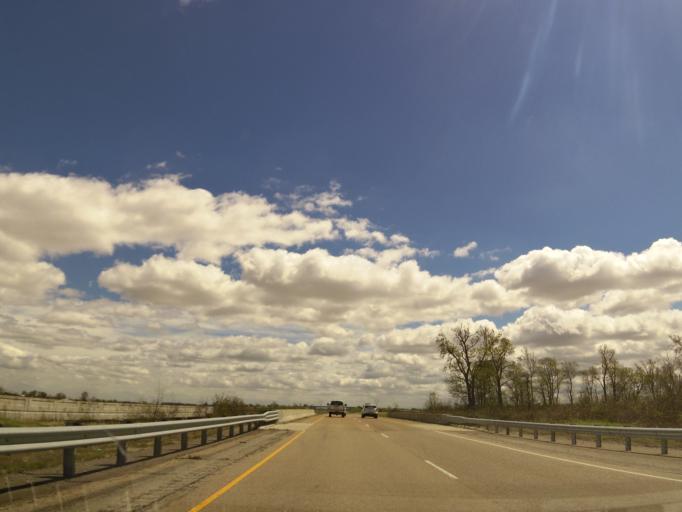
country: US
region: Arkansas
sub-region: Craighead County
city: Bay
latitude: 35.7796
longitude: -90.5931
